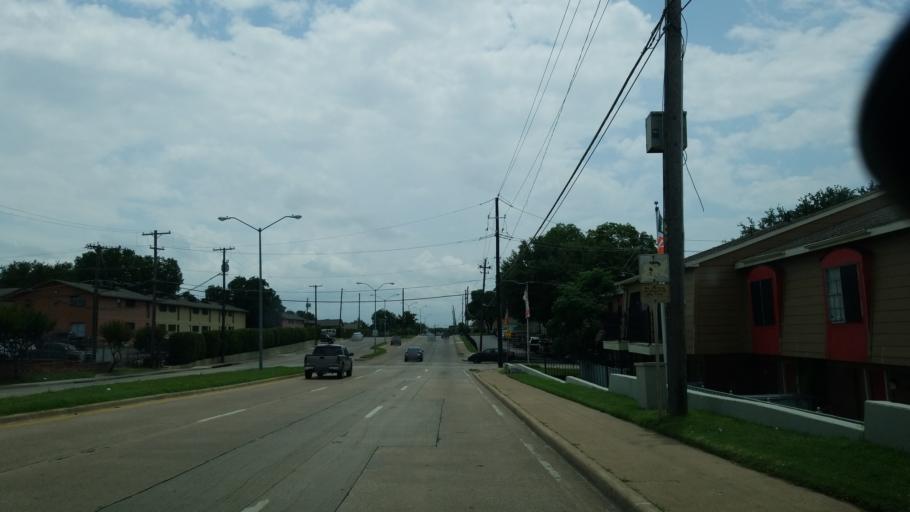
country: US
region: Texas
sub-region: Dallas County
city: Farmers Branch
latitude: 32.8722
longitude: -96.8648
